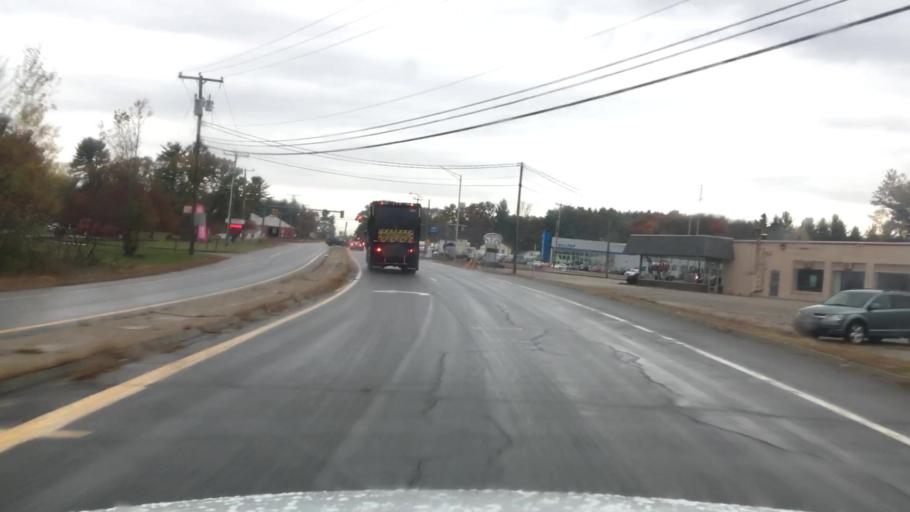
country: US
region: New Hampshire
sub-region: Strafford County
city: Somersworth
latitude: 43.2639
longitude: -70.9056
